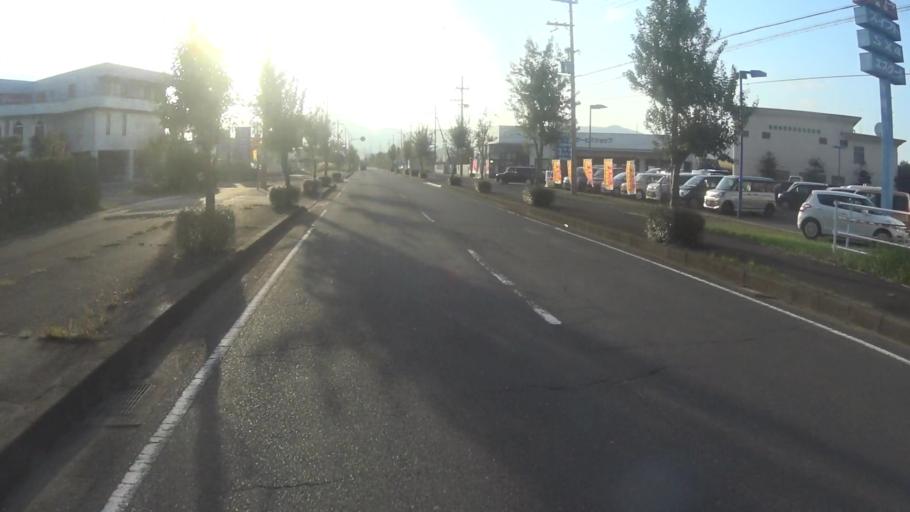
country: JP
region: Kyoto
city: Miyazu
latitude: 35.6094
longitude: 135.0676
